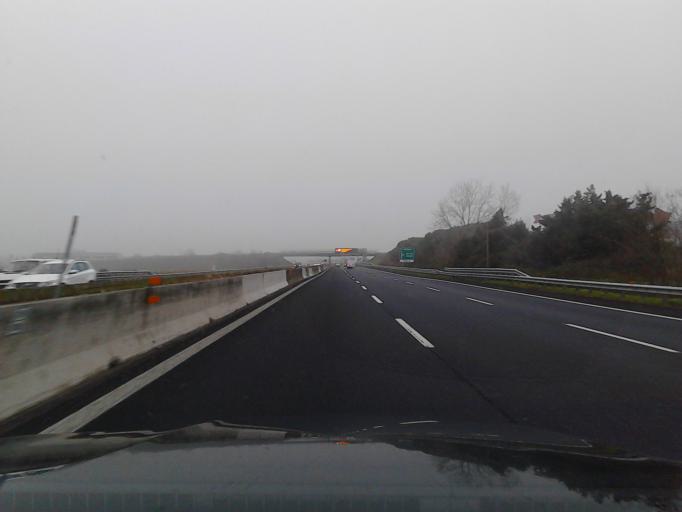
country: IT
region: Emilia-Romagna
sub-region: Forli-Cesena
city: Gatteo-Sant'Angelo
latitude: 44.1263
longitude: 12.3812
